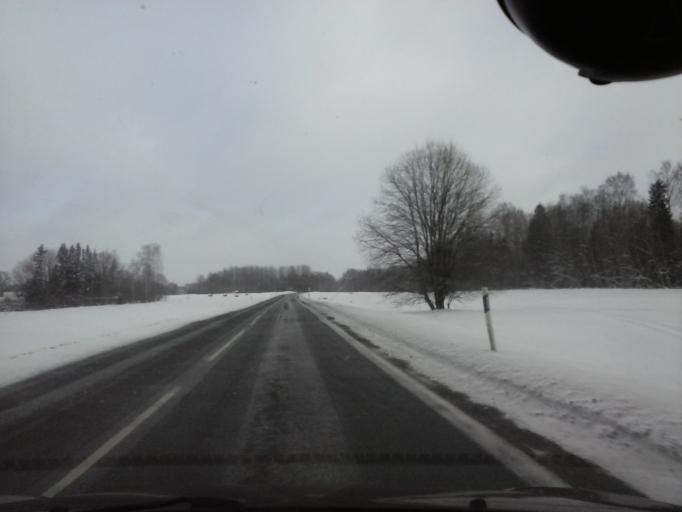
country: EE
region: Viljandimaa
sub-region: Viljandi linn
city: Viljandi
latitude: 58.3600
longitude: 25.4080
